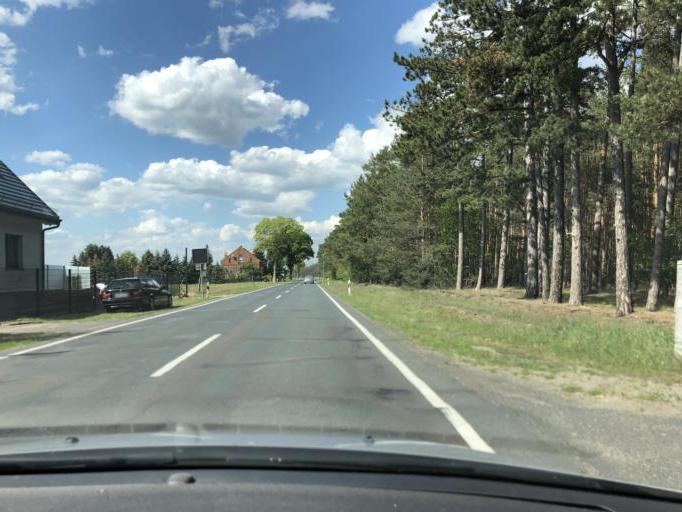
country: DE
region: Brandenburg
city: Spreenhagen
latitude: 52.3302
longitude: 13.8981
